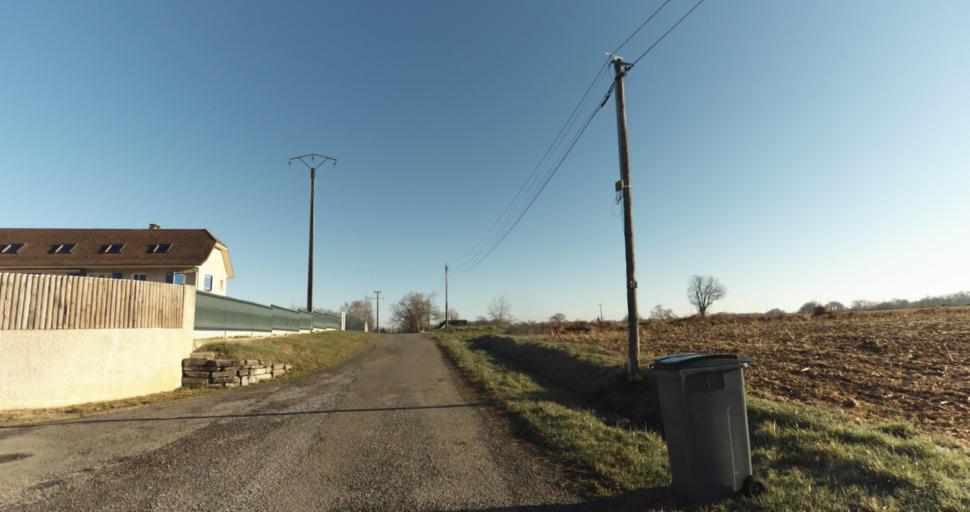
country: FR
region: Aquitaine
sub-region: Departement des Pyrenees-Atlantiques
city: Morlaas
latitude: 43.3202
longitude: -0.2510
